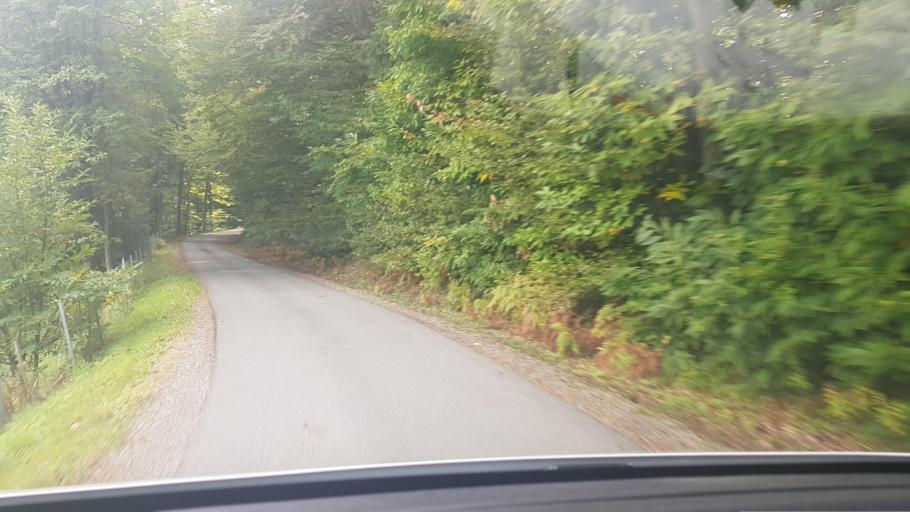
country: AT
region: Styria
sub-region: Politischer Bezirk Leibnitz
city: Sankt Johann im Saggautal
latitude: 46.7090
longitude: 15.4320
